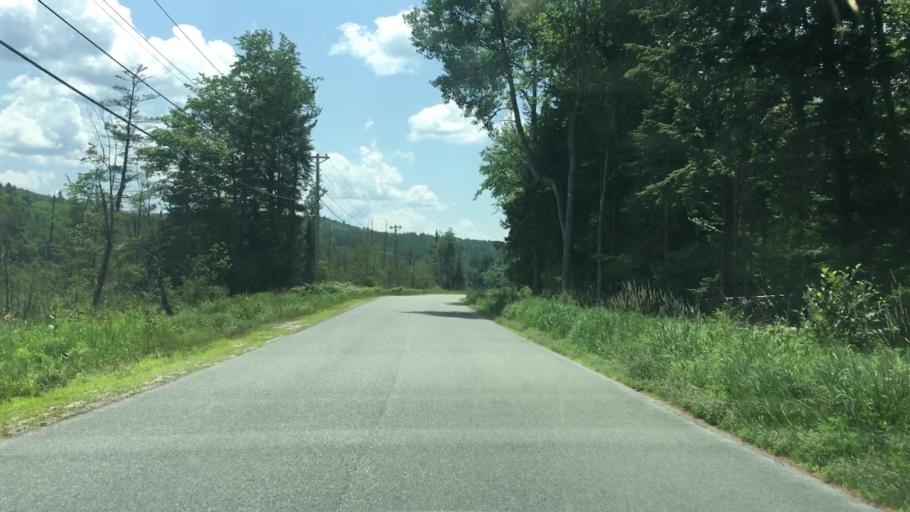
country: US
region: New Hampshire
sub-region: Grafton County
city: Enfield
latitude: 43.6833
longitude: -72.0934
